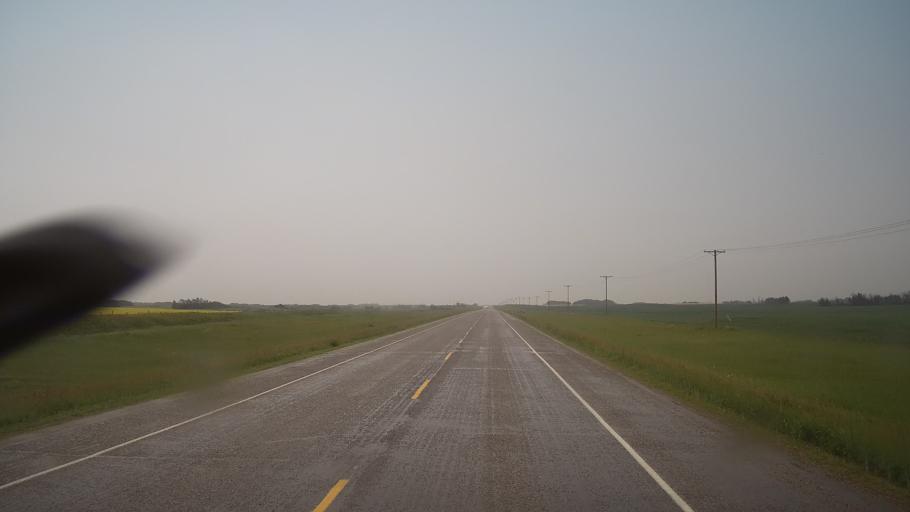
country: CA
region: Saskatchewan
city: Biggar
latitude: 52.1538
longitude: -108.2466
